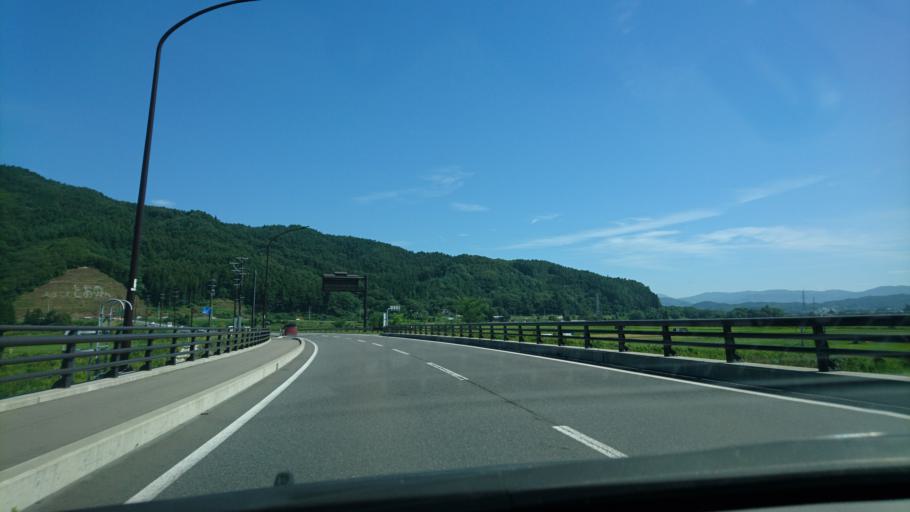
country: JP
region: Iwate
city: Tono
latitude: 39.3278
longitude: 141.5090
